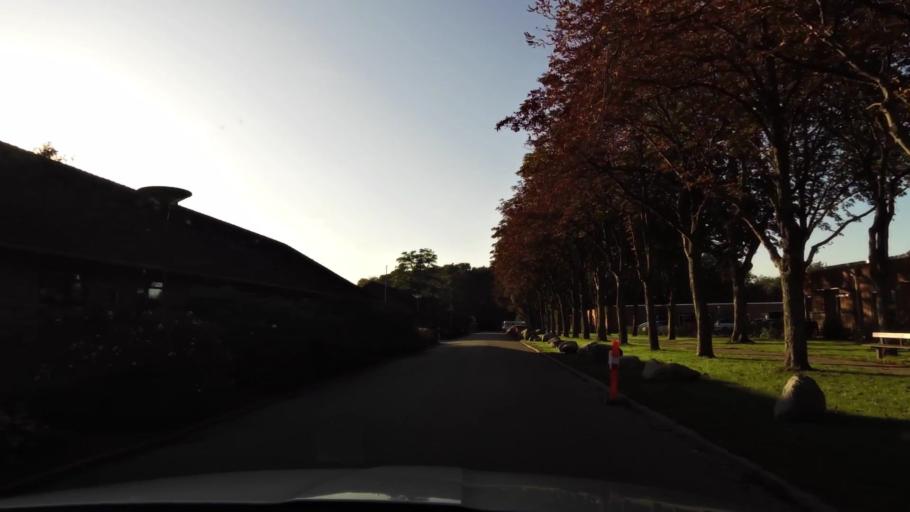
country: DK
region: Capital Region
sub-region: Lyngby-Tarbaek Kommune
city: Kongens Lyngby
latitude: 55.7519
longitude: 12.5097
